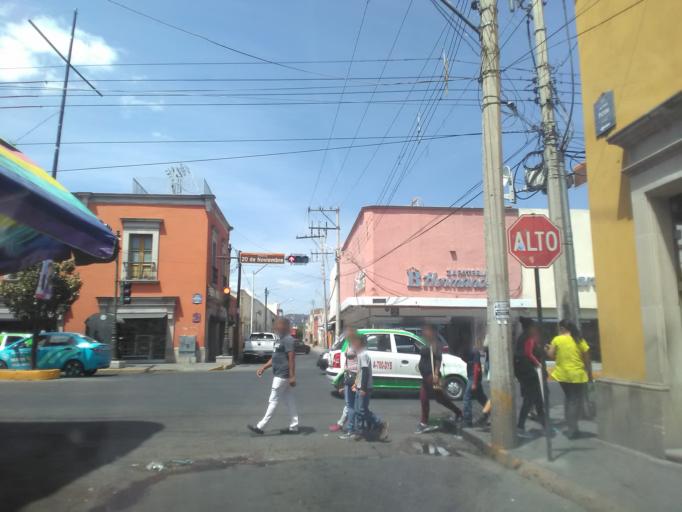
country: MX
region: Durango
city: Victoria de Durango
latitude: 24.0252
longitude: -104.6666
